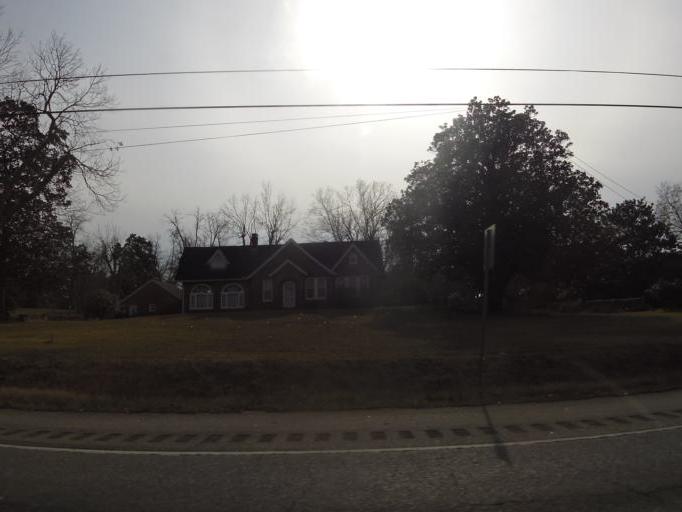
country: US
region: Alabama
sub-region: Houston County
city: Cowarts
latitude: 31.1951
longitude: -85.3285
